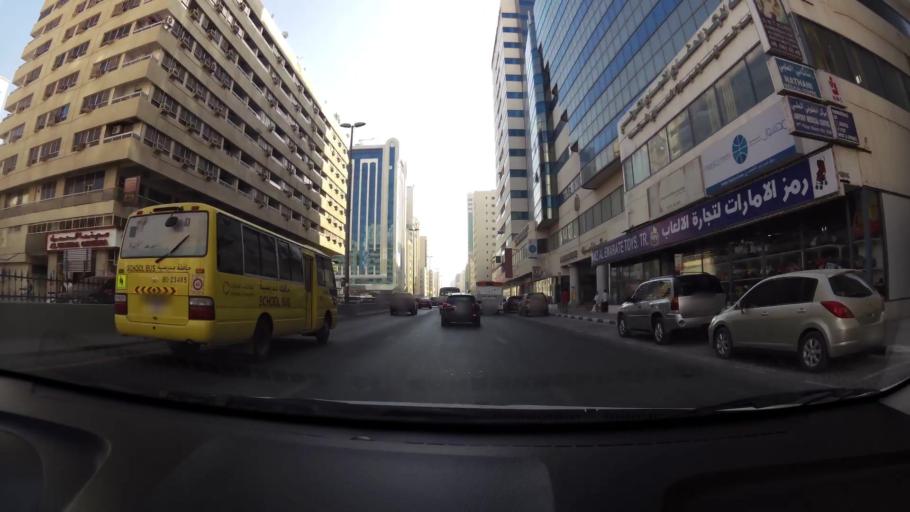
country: AE
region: Ash Shariqah
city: Sharjah
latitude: 25.3646
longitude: 55.3928
